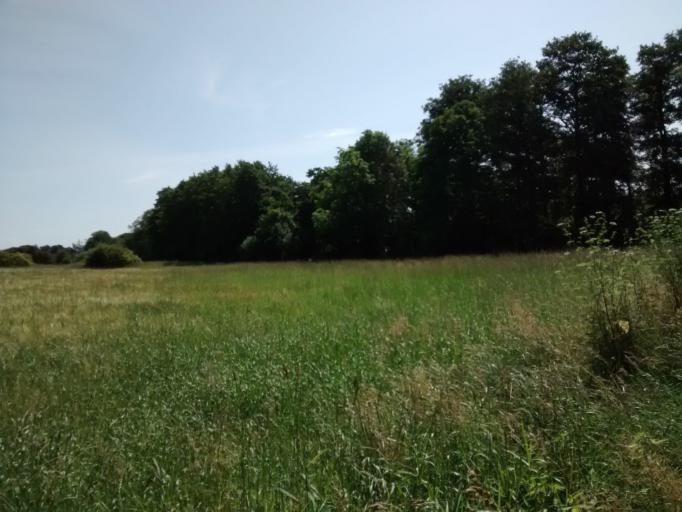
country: DK
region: Zealand
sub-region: Soro Kommune
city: Soro
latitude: 55.4529
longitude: 11.5850
